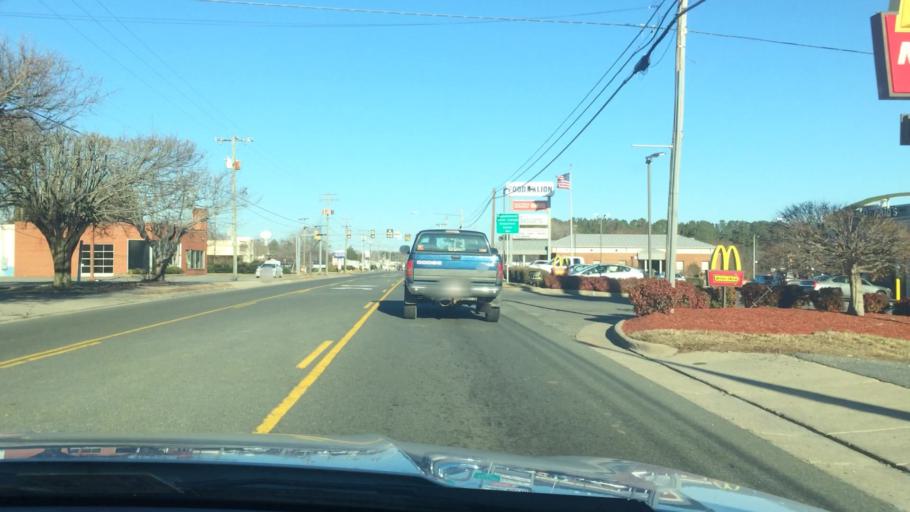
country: US
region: Virginia
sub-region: Lancaster County
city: Kilmarnock
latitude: 37.7189
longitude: -76.3837
